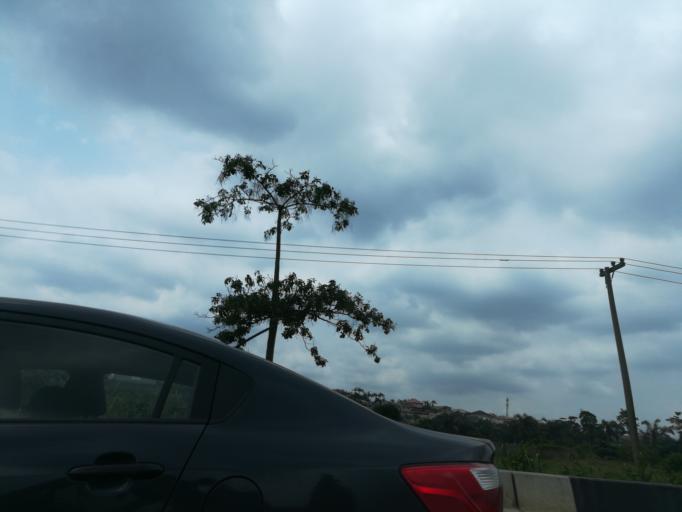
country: NG
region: Lagos
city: Ojota
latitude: 6.5791
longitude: 3.3948
